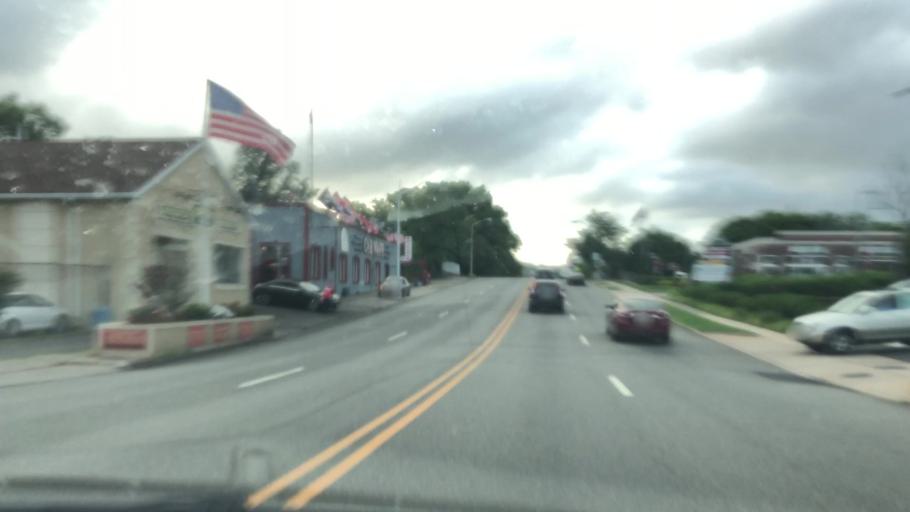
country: US
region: New Jersey
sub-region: Essex County
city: Glen Ridge
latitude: 40.8053
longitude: -74.2081
